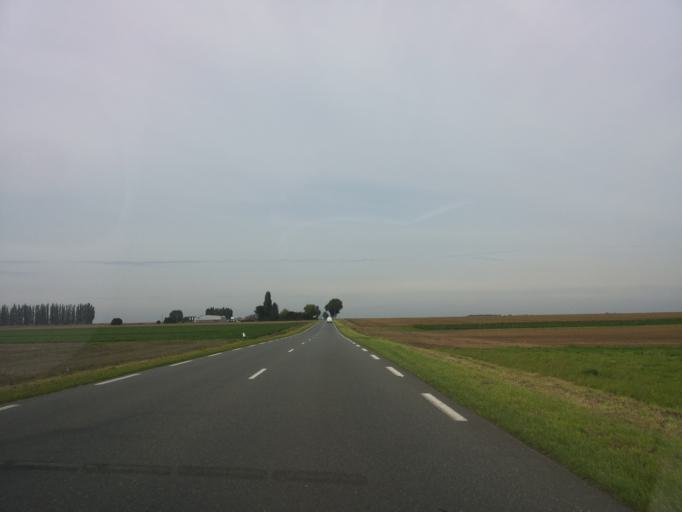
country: FR
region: Nord-Pas-de-Calais
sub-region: Departement du Nord
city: Raillencourt-Sainte-Olle
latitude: 50.1958
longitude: 3.1460
